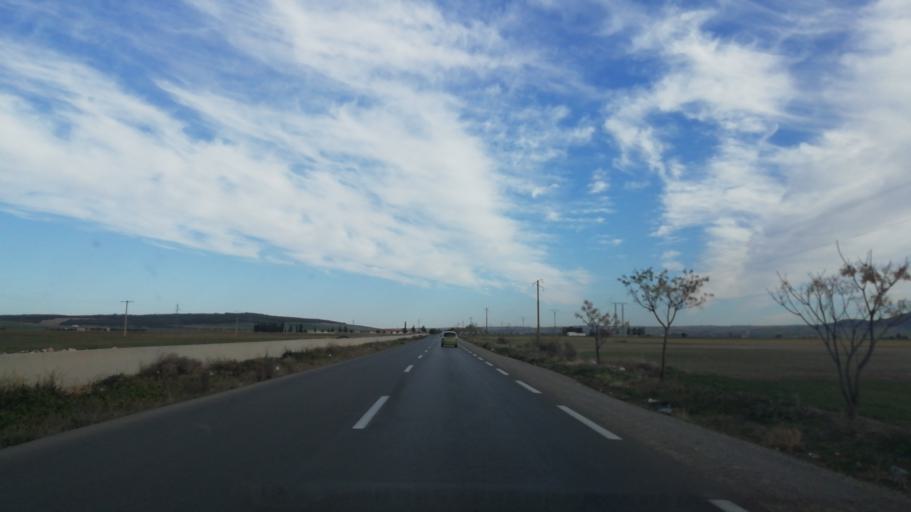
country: DZ
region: Sidi Bel Abbes
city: Sidi Bel Abbes
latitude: 35.1792
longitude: -0.4746
